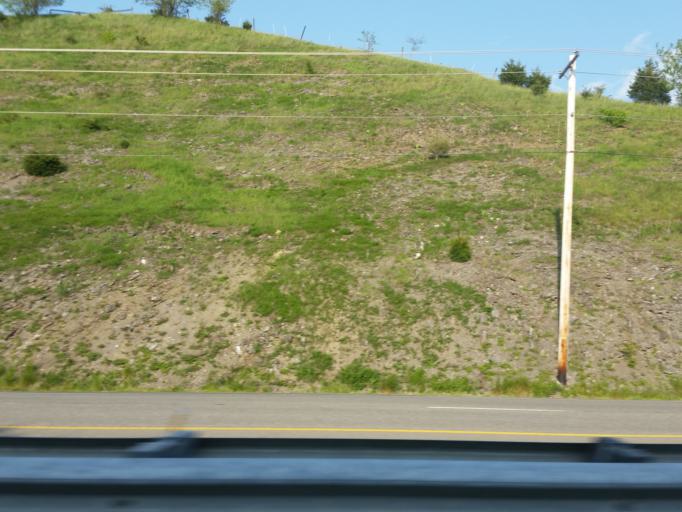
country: US
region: Virginia
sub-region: Tazewell County
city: Claypool Hill
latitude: 37.0265
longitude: -81.7975
